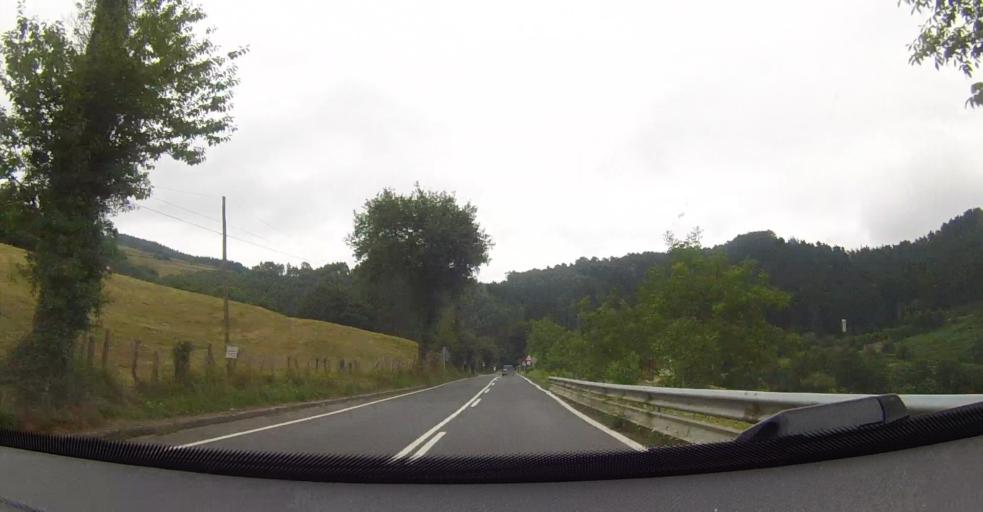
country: ES
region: Basque Country
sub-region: Bizkaia
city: Balmaseda
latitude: 43.2423
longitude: -3.3045
